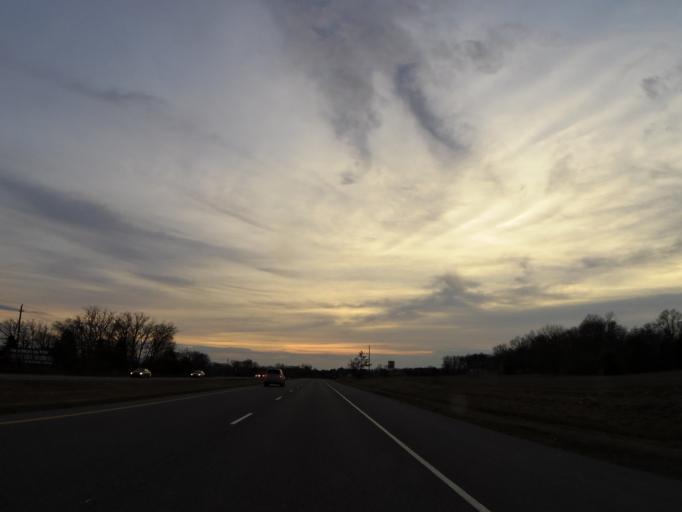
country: US
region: Tennessee
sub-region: Monroe County
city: Madisonville
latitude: 35.4679
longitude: -84.4195
